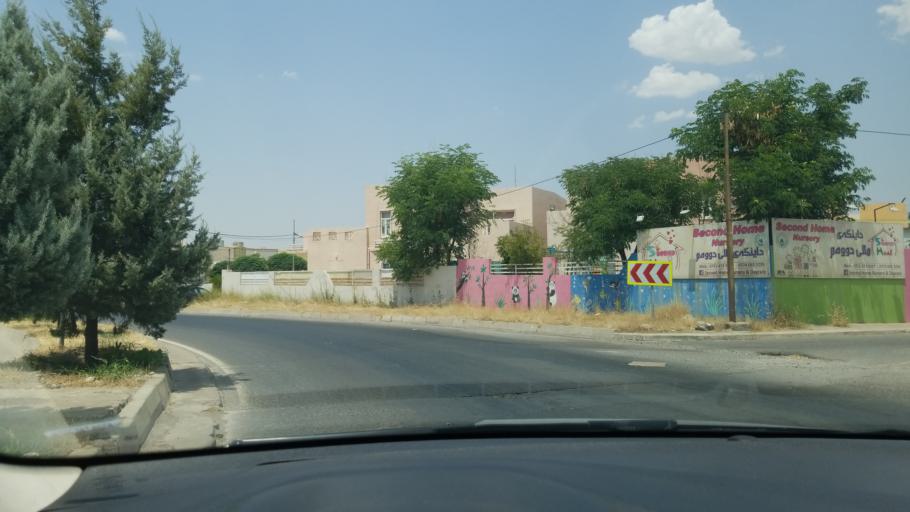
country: IQ
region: Arbil
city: Erbil
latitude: 36.1704
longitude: 44.0594
